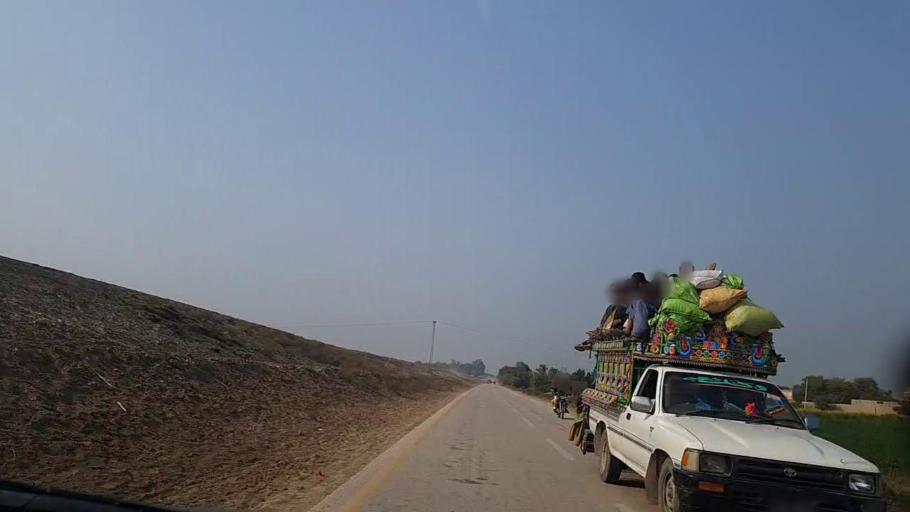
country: PK
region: Sindh
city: Sann
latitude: 26.1611
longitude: 68.1141
